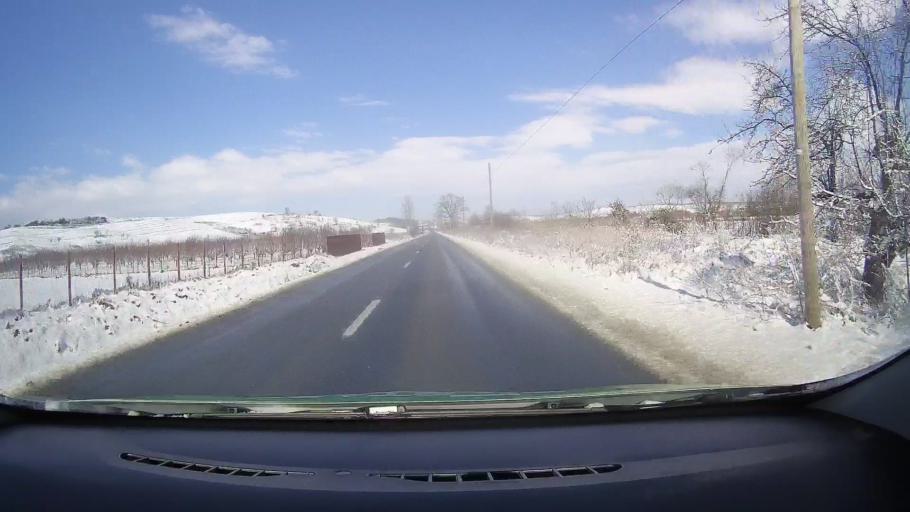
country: RO
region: Sibiu
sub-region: Comuna Nocrich
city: Nocrich
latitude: 45.8771
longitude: 24.4516
